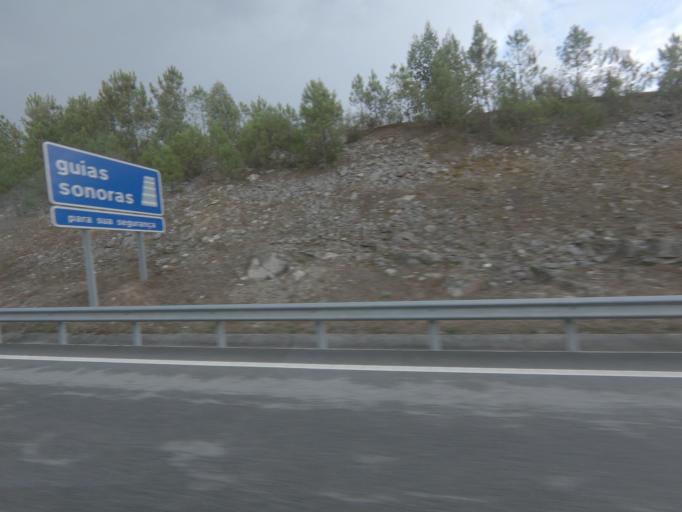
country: PT
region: Viseu
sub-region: Viseu
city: Abraveses
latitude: 40.6862
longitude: -7.9672
